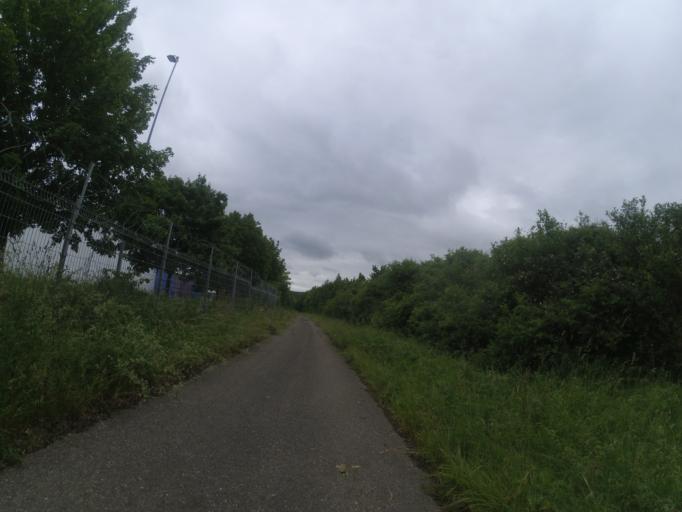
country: DE
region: Baden-Wuerttemberg
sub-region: Tuebingen Region
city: Langenau
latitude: 48.4963
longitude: 10.0857
